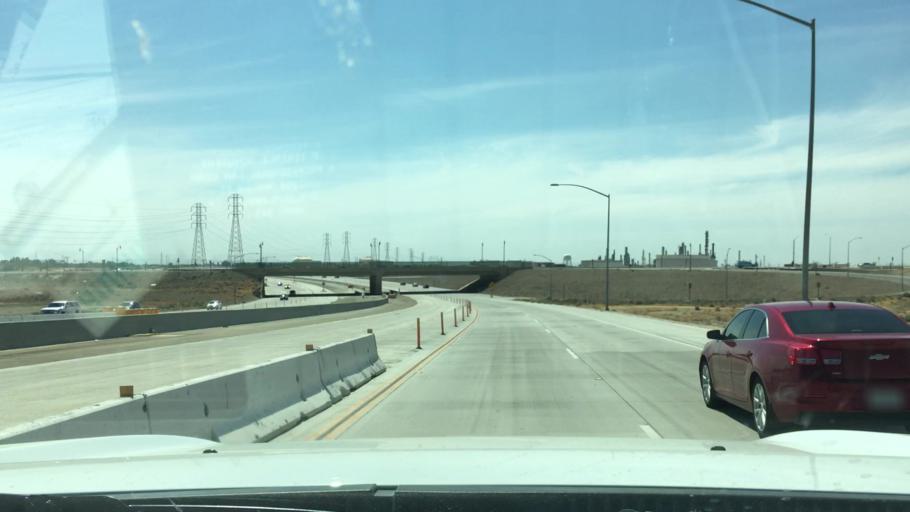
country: US
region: California
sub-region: Kern County
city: Bakersfield
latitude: 35.3719
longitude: -119.0628
